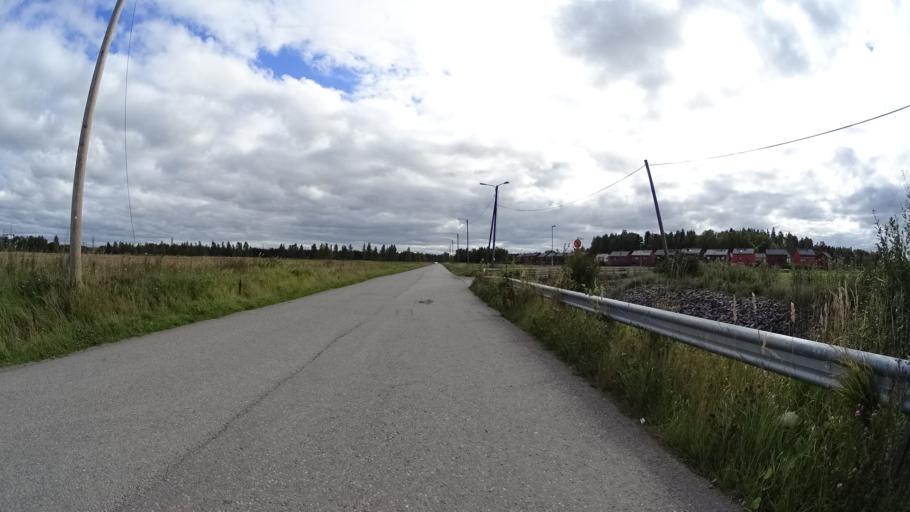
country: FI
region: Uusimaa
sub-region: Helsinki
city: Vantaa
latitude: 60.2671
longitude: 24.9580
